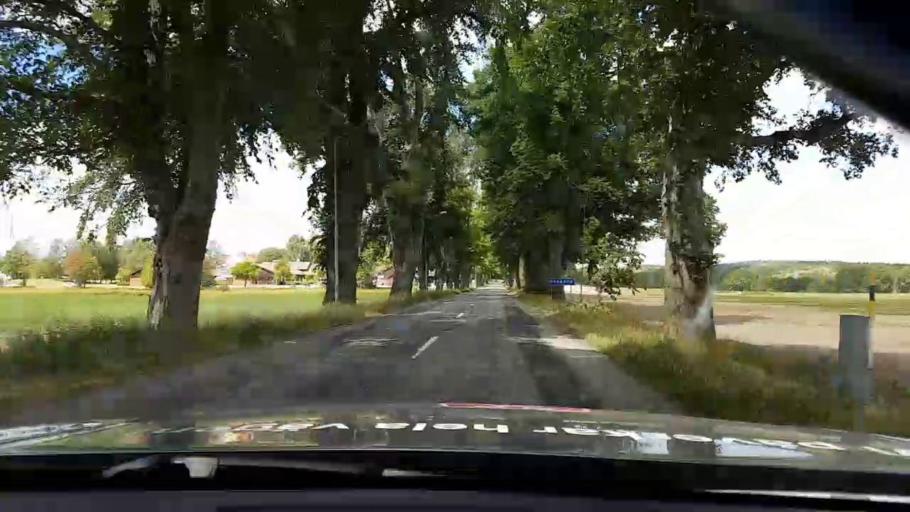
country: SE
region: Kalmar
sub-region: Vasterviks Kommun
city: Forserum
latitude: 58.0098
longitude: 16.4810
